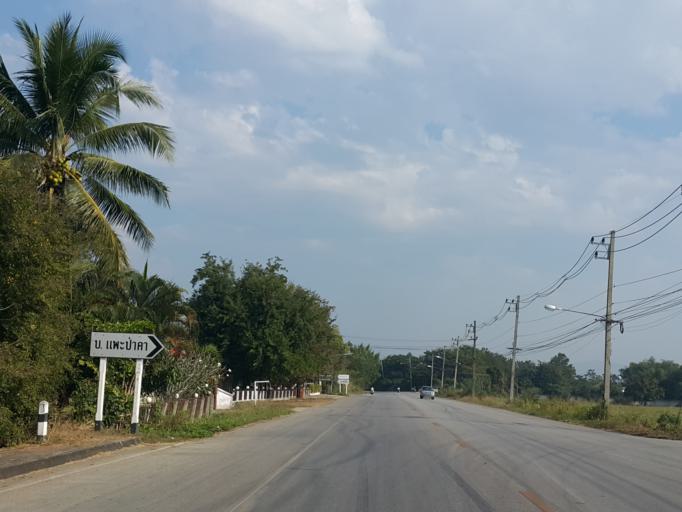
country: TH
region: Chiang Mai
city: San Kamphaeng
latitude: 18.8271
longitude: 99.1267
